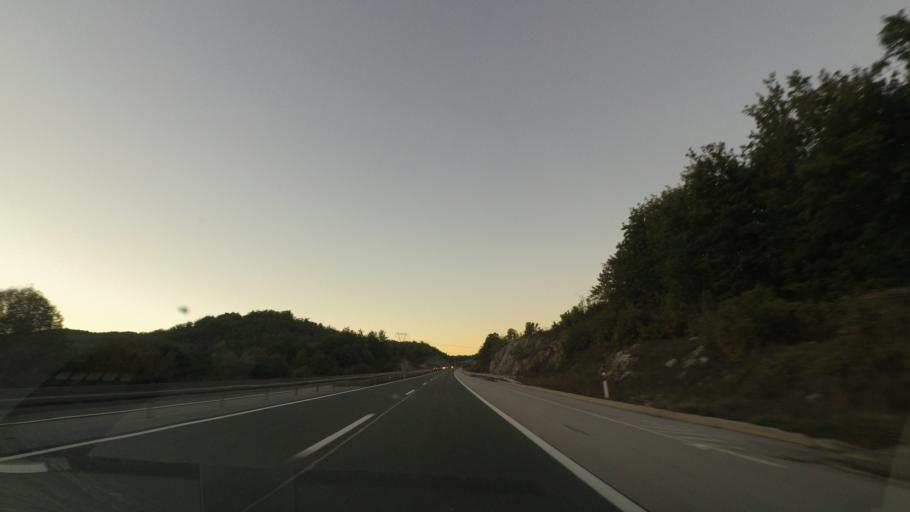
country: HR
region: Zadarska
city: Obrovac
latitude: 44.3529
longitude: 15.6420
